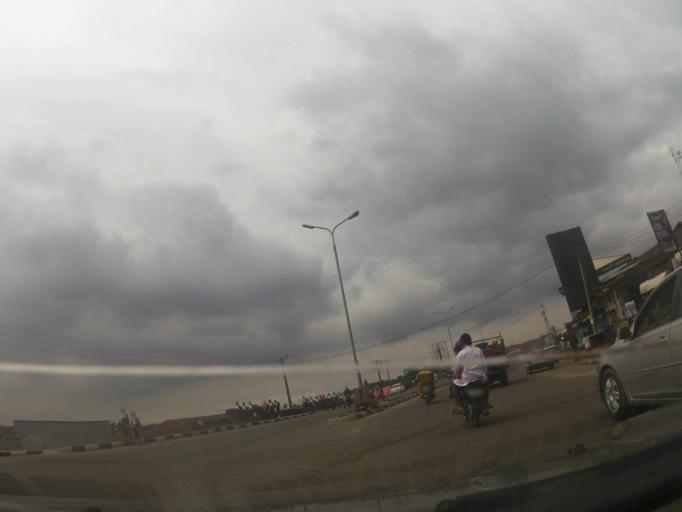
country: NG
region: Oyo
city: Ibadan
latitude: 7.4073
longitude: 3.8893
